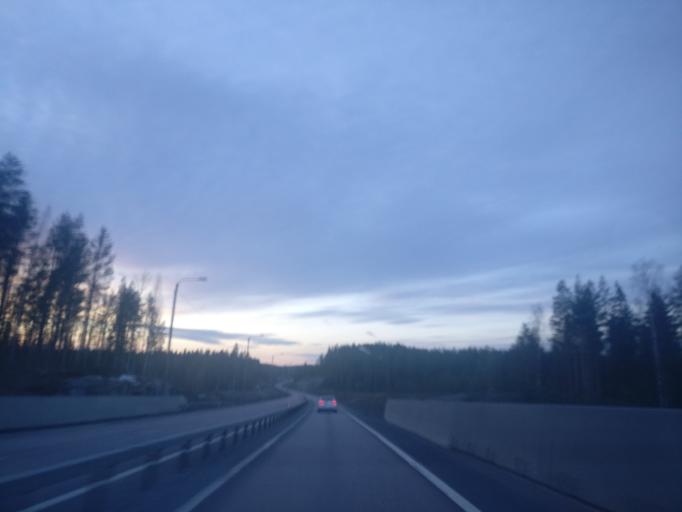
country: FI
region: Central Finland
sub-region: Jyvaeskylae
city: Saeynaetsalo
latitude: 62.1903
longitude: 25.9020
